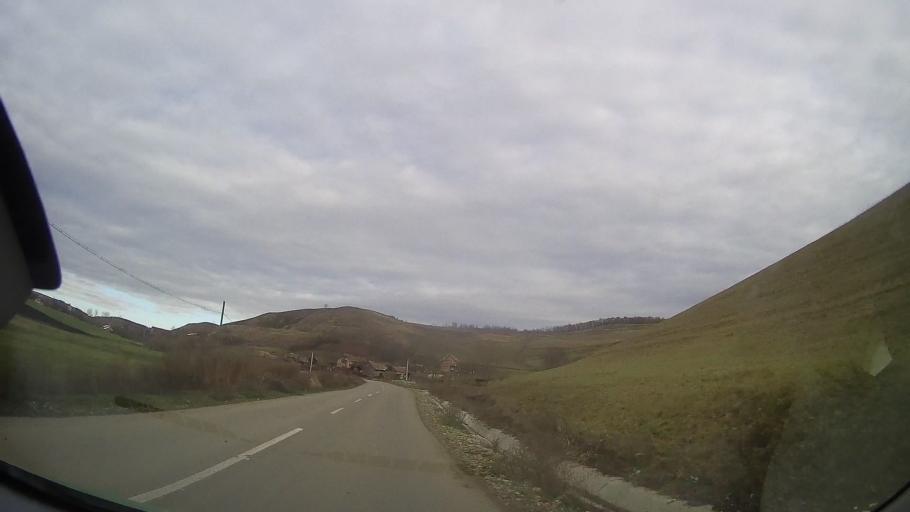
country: RO
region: Bistrita-Nasaud
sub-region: Comuna Micestii de Campie
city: Micestii de Campie
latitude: 46.8289
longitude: 24.3062
